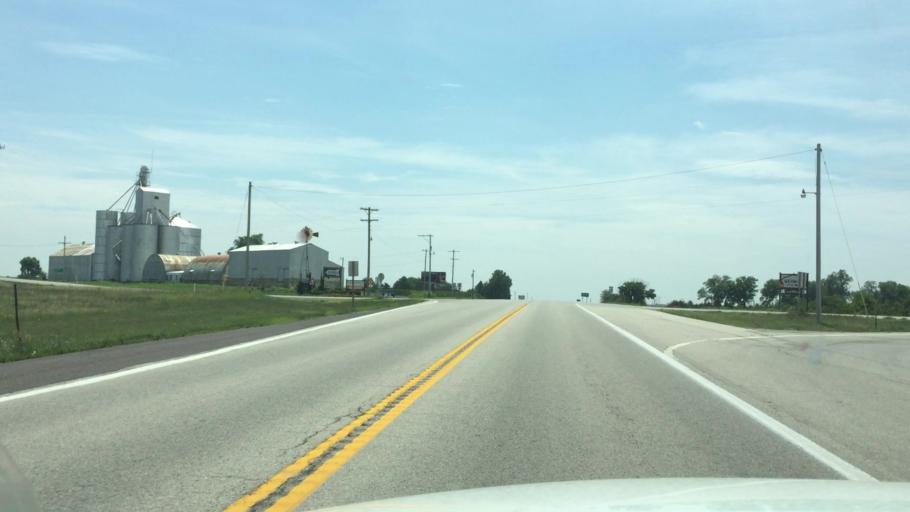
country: US
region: Kansas
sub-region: Jackson County
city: Holton
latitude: 39.6144
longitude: -95.7312
